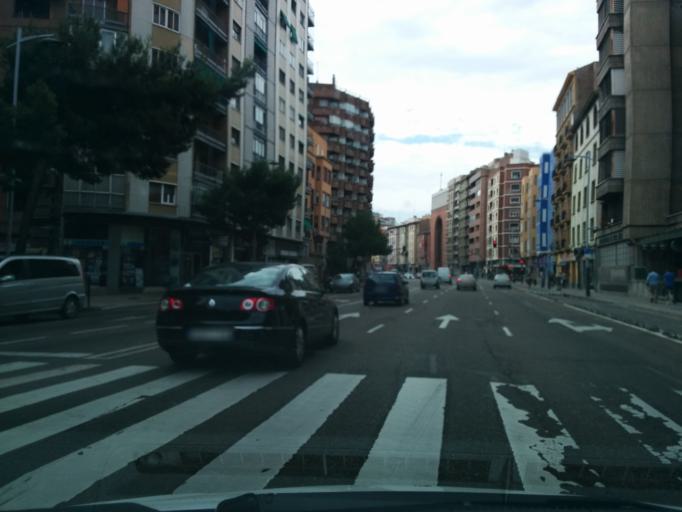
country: ES
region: Aragon
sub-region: Provincia de Zaragoza
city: Delicias
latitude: 41.6474
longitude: -0.8939
